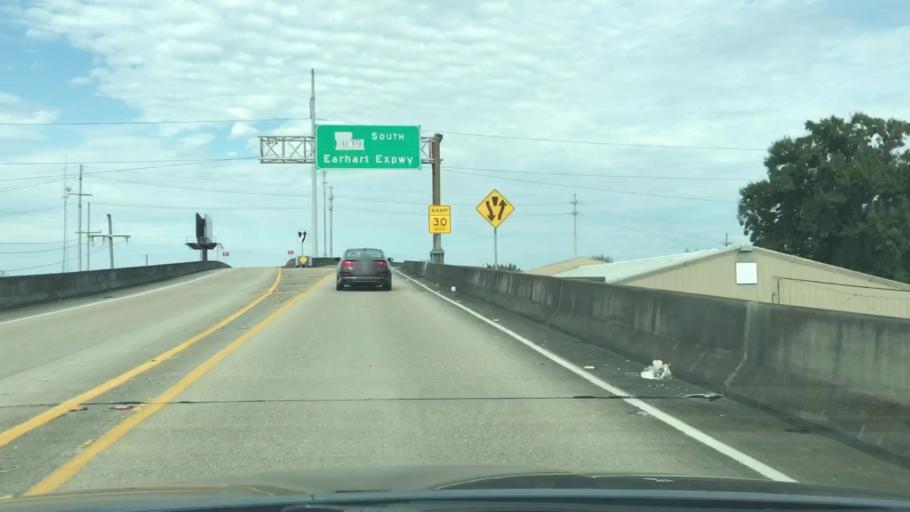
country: US
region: Louisiana
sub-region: Jefferson Parish
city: Jefferson
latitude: 29.9681
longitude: -90.1458
